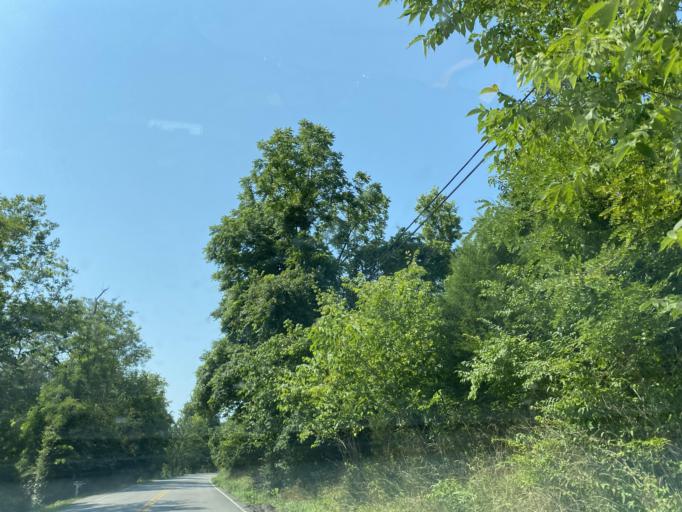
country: US
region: Kentucky
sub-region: Campbell County
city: Claryville
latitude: 38.8597
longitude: -84.4623
